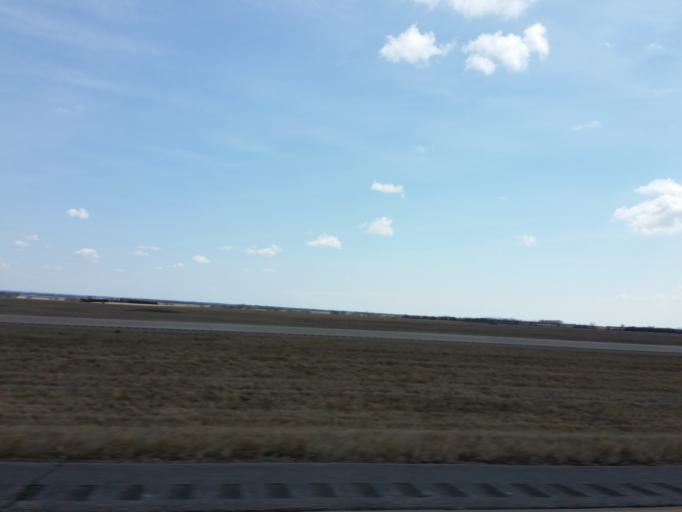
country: US
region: South Dakota
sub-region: Roberts County
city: Sisseton
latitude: 45.4303
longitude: -96.9994
